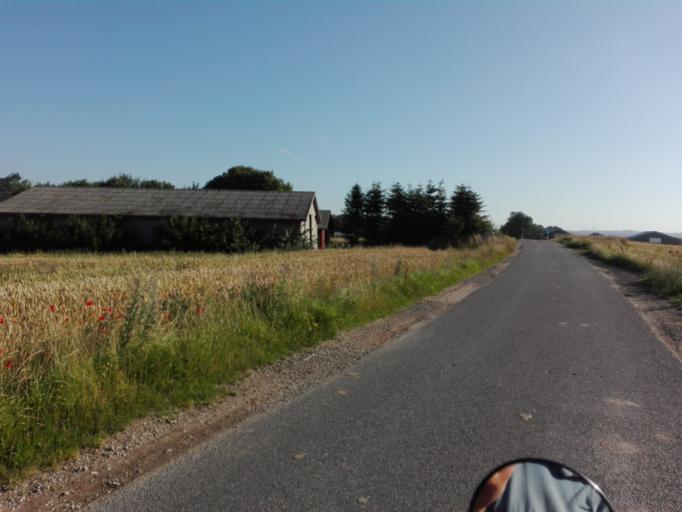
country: DK
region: Central Jutland
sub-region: Arhus Kommune
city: Marslet
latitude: 56.0594
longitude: 10.1449
